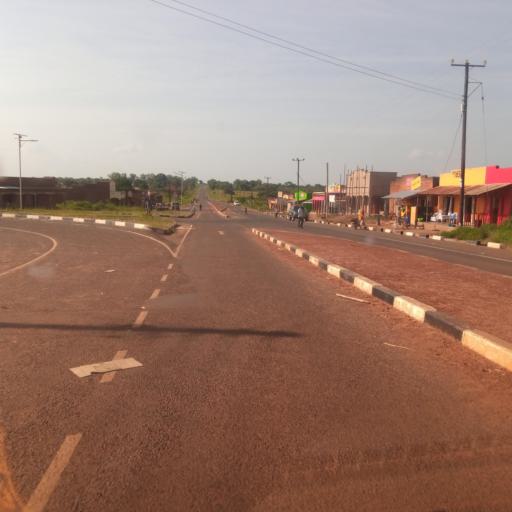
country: UG
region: Northern Region
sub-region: Kitgum District
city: Kitgum
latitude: 3.1436
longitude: 32.9139
